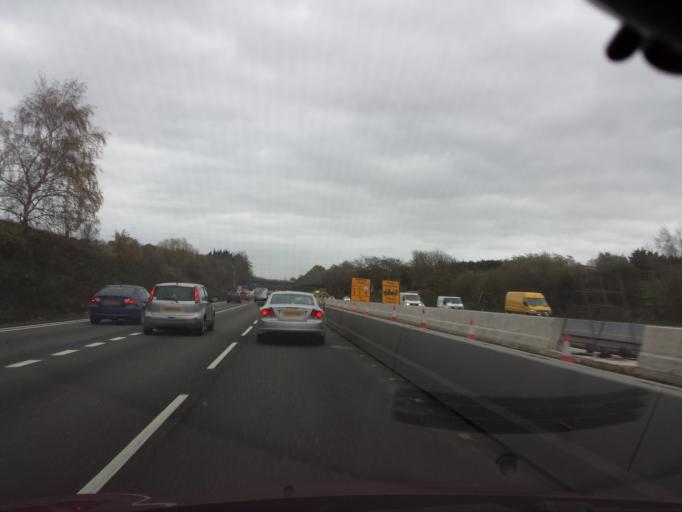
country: GB
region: England
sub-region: Surrey
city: Virginia Water
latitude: 51.3938
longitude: -0.5591
